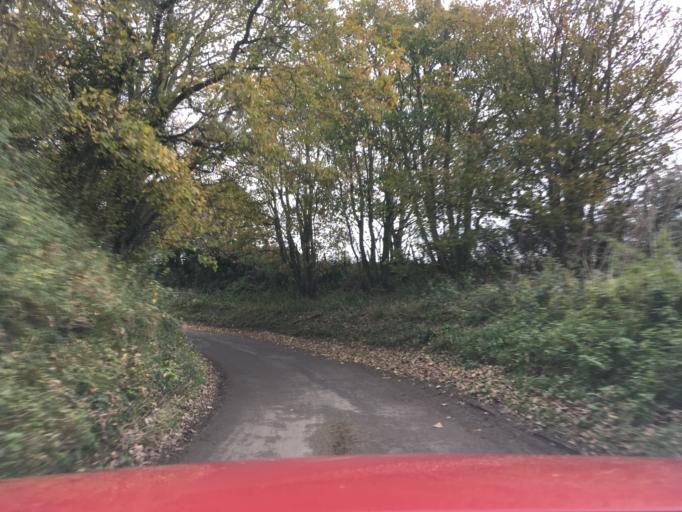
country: GB
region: England
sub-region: Somerset
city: Ilminster
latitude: 50.9529
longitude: -2.8722
